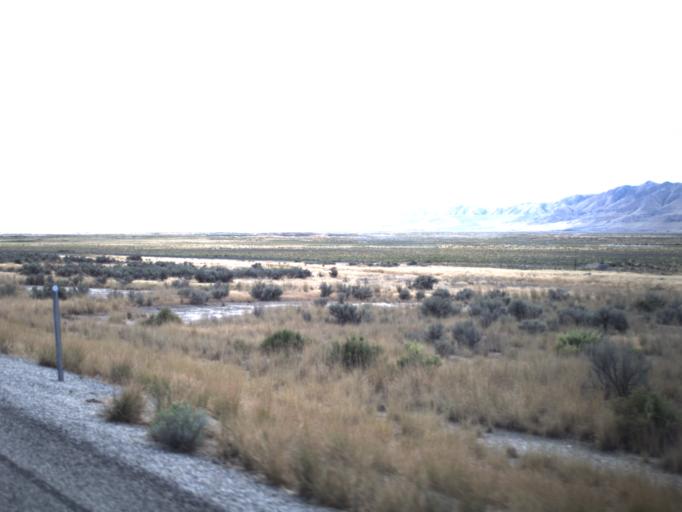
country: US
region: Utah
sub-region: Box Elder County
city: Tremonton
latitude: 41.6385
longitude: -112.4257
